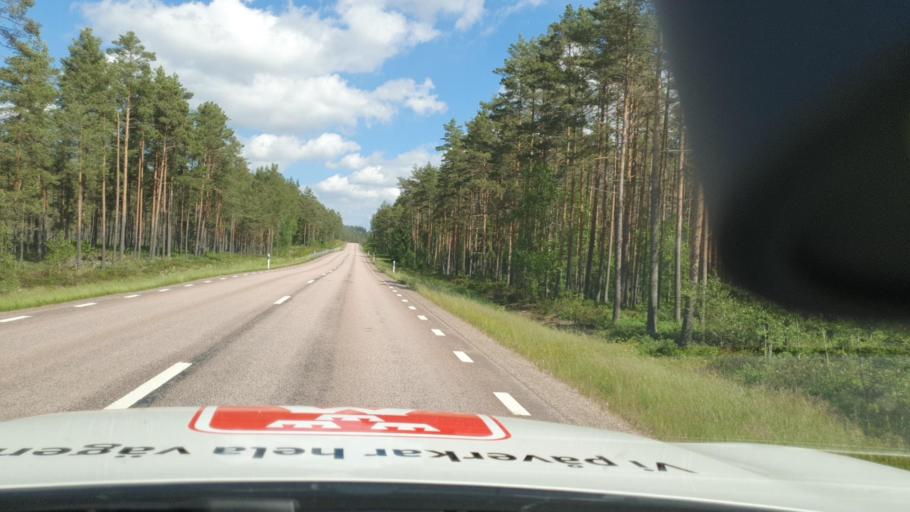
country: SE
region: Vaermland
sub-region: Karlstads Kommun
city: Molkom
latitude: 59.6092
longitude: 13.8734
